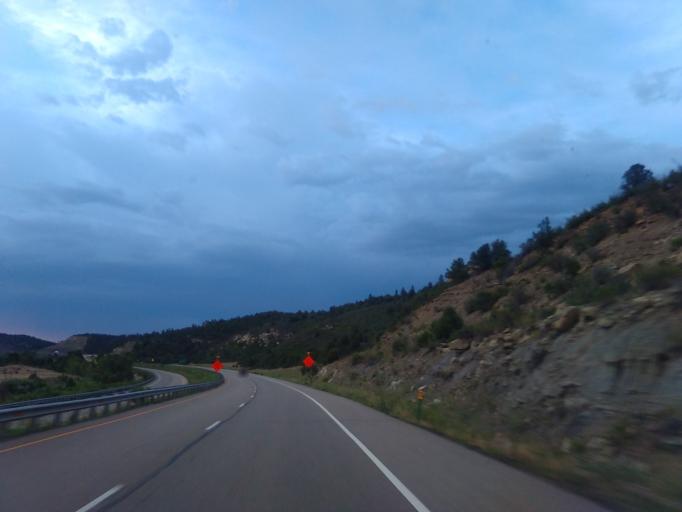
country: US
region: Colorado
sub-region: Las Animas County
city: Trinidad
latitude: 37.0706
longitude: -104.5175
